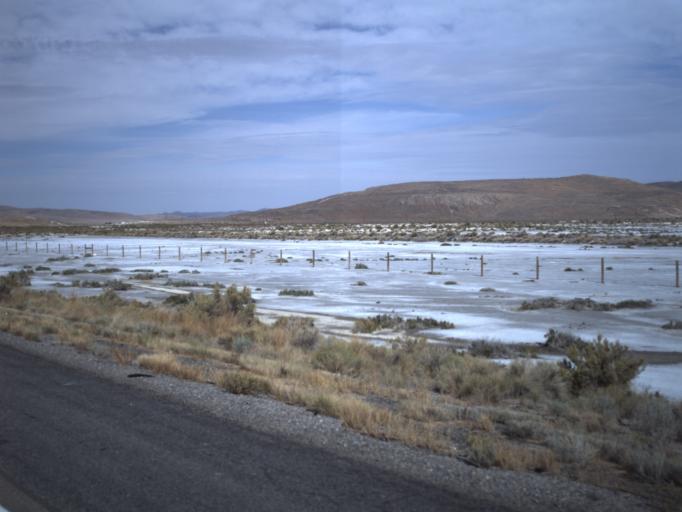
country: US
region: Utah
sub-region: Tooele County
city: Grantsville
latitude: 40.7566
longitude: -112.7577
